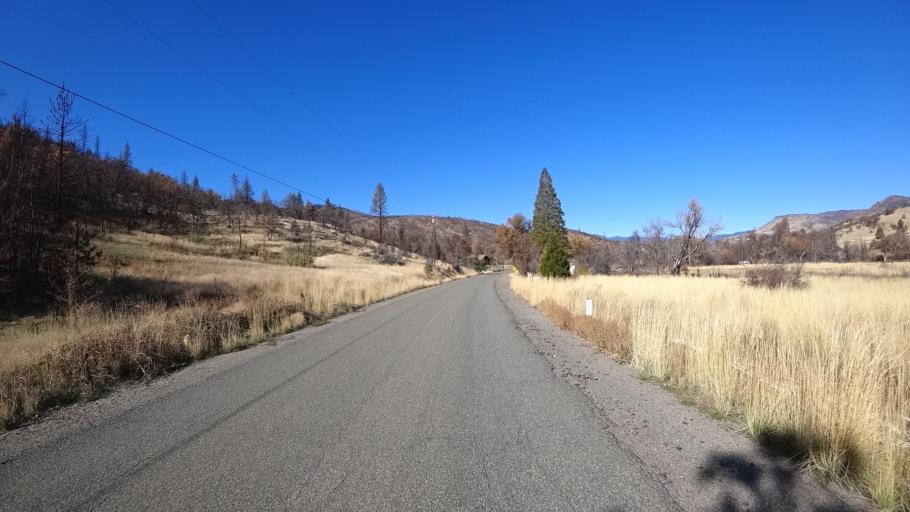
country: US
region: California
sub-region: Siskiyou County
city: Yreka
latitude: 41.9305
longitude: -122.5871
